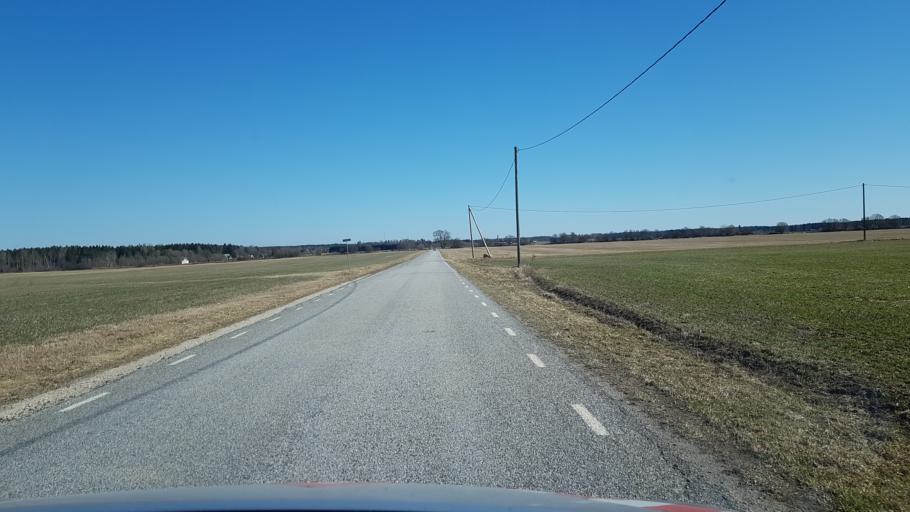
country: EE
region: Laeaene-Virumaa
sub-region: Viru-Nigula vald
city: Kunda
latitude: 59.4062
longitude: 26.5372
